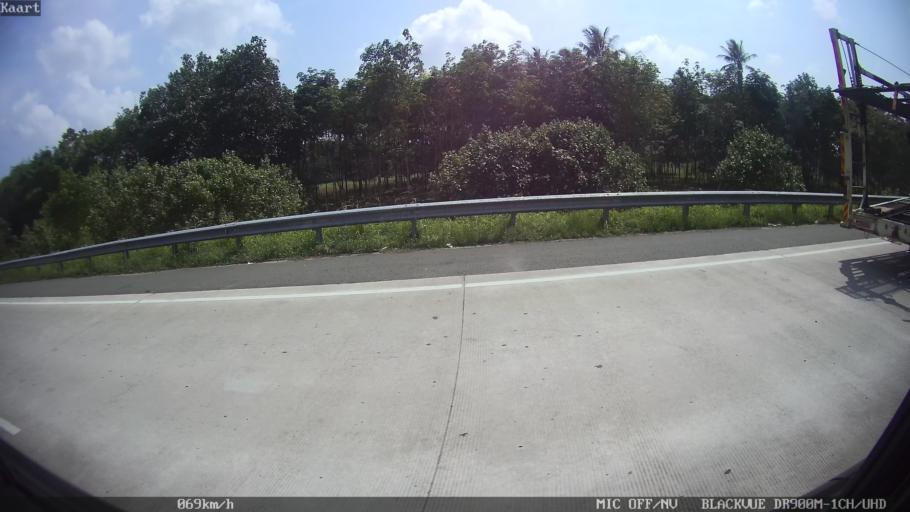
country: ID
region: Lampung
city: Natar
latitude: -5.3046
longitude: 105.2455
